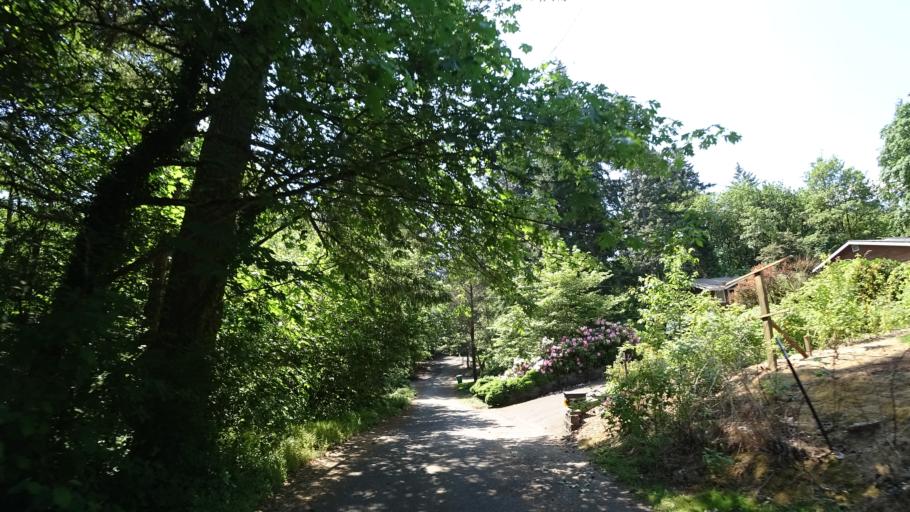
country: US
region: Oregon
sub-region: Clackamas County
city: Lake Oswego
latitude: 45.4428
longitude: -122.7107
